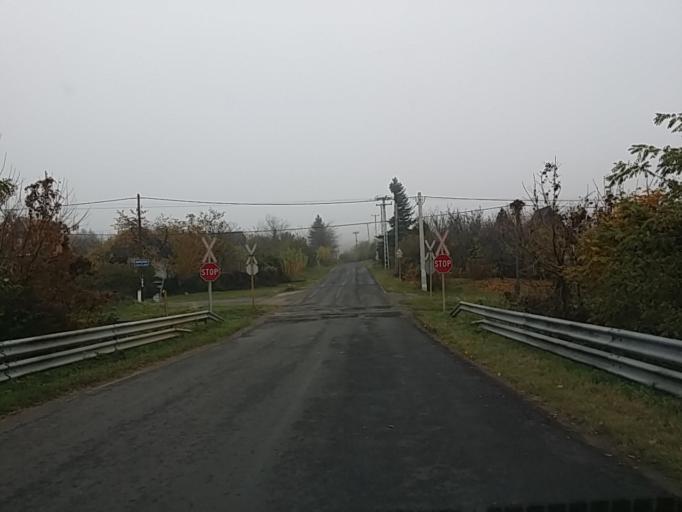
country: HU
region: Heves
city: Gyongyossolymos
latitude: 47.8115
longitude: 19.9574
